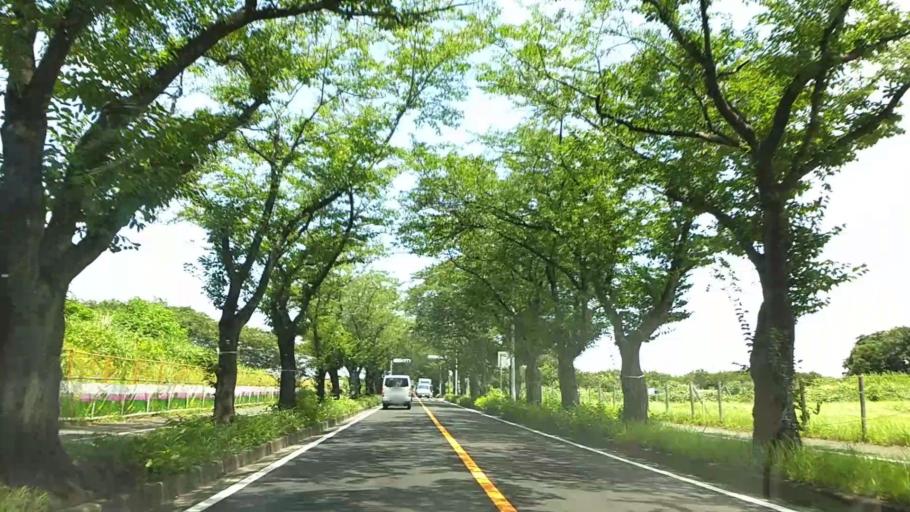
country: JP
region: Kanagawa
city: Minami-rinkan
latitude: 35.4888
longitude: 139.4803
